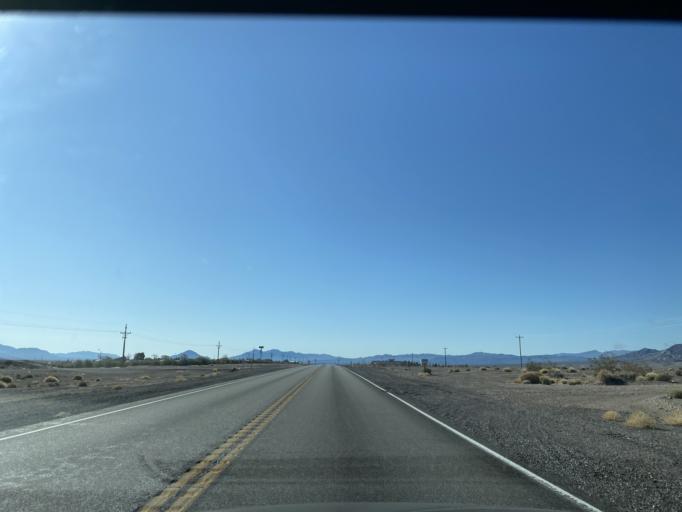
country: US
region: Nevada
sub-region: Nye County
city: Pahrump
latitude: 36.4225
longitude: -116.4222
